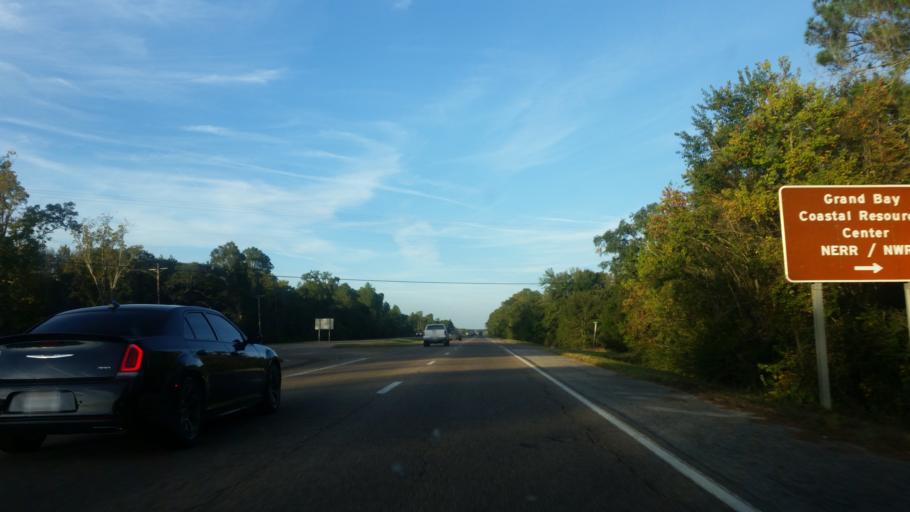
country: US
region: Mississippi
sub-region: Jackson County
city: Helena
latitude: 30.4431
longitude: -88.4310
